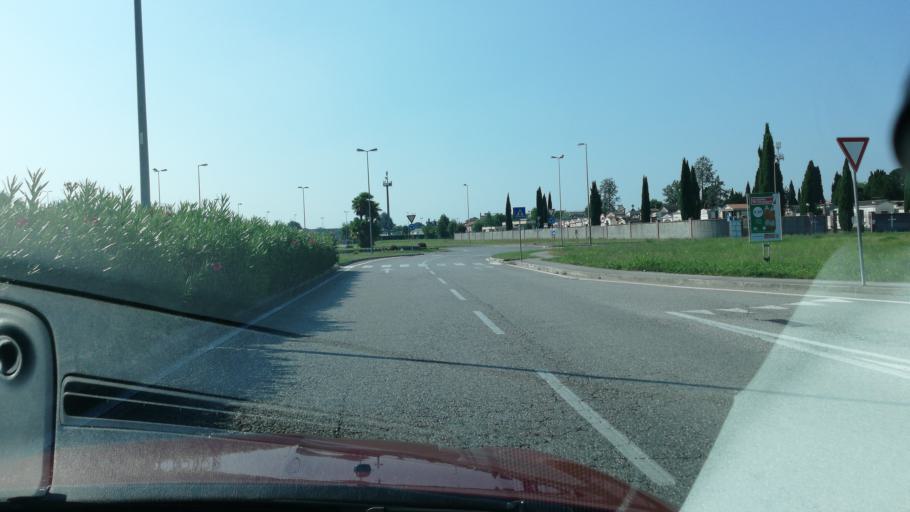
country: IT
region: Friuli Venezia Giulia
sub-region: Provincia di Udine
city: Latisana
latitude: 45.7765
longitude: 13.0030
